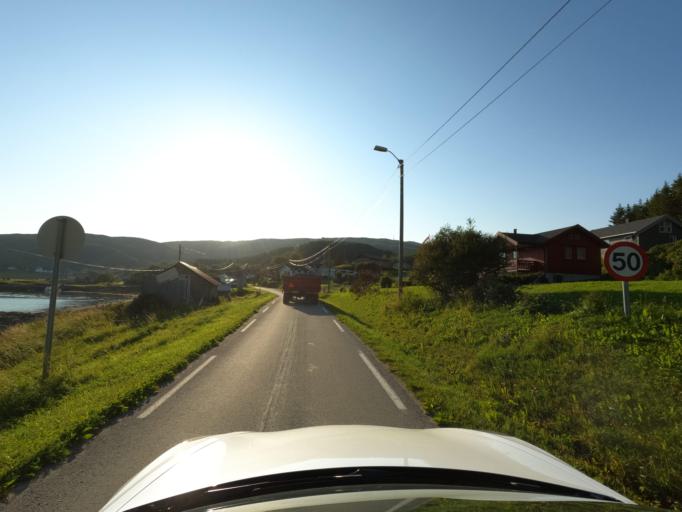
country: NO
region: Troms
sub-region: Skanland
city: Evenskjer
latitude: 68.4556
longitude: 16.6043
